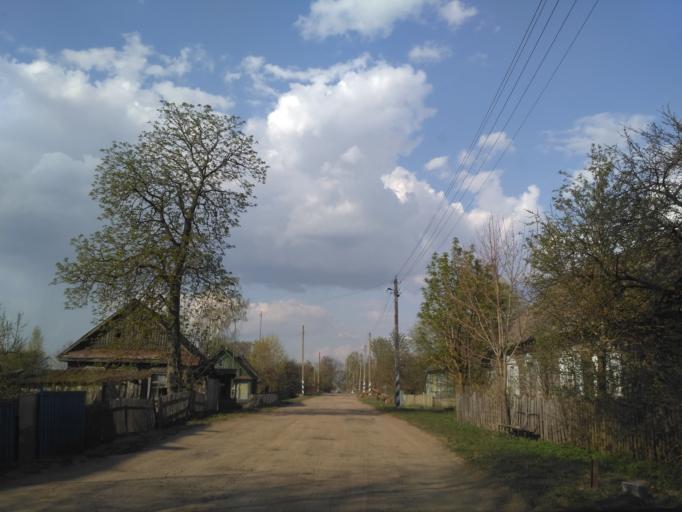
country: BY
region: Minsk
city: Khalopyenichy
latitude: 54.5030
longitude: 28.8480
